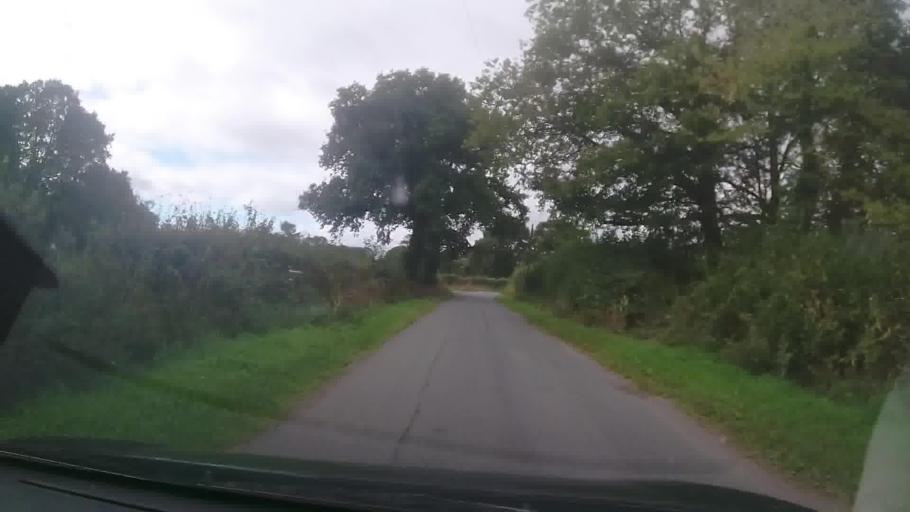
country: GB
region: England
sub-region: Shropshire
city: Prees
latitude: 52.8808
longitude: -2.6408
